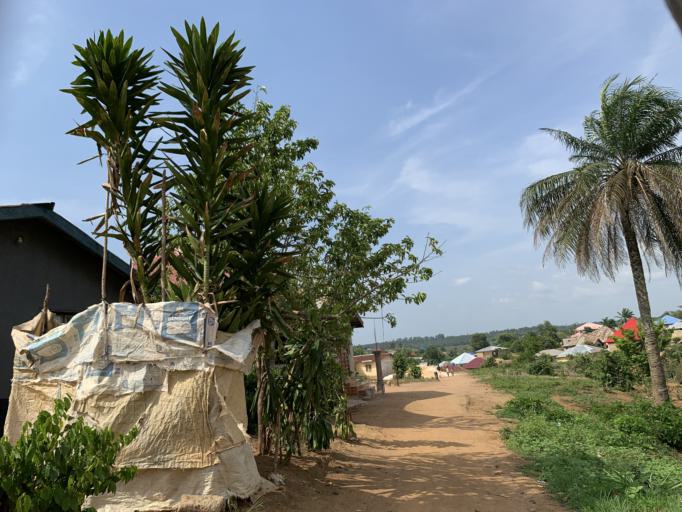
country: SL
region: Western Area
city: Waterloo
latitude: 8.3494
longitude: -13.0406
